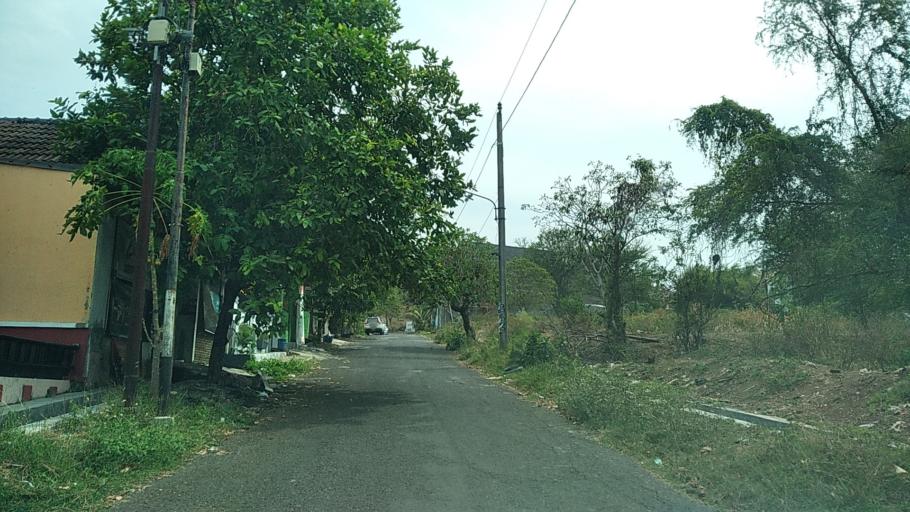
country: ID
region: Central Java
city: Semarang
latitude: -7.0414
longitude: 110.4422
